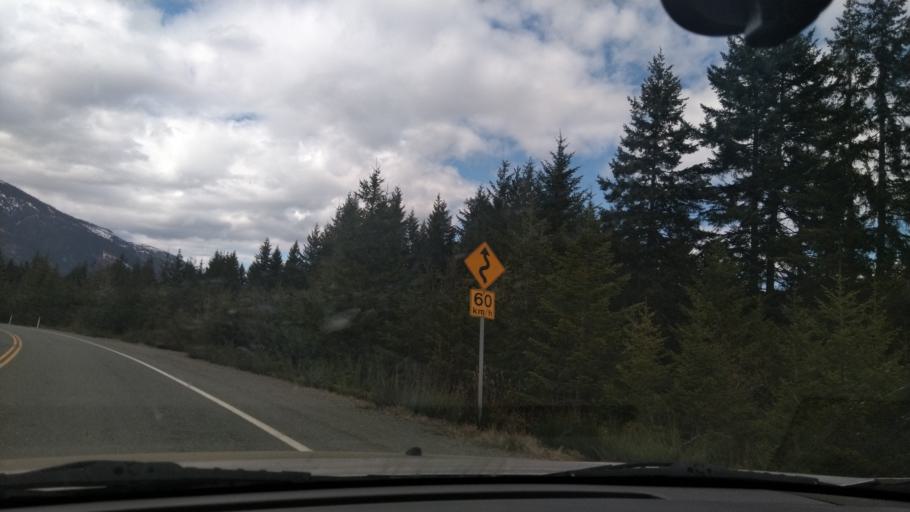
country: CA
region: British Columbia
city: Campbell River
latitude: 49.8677
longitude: -125.6472
